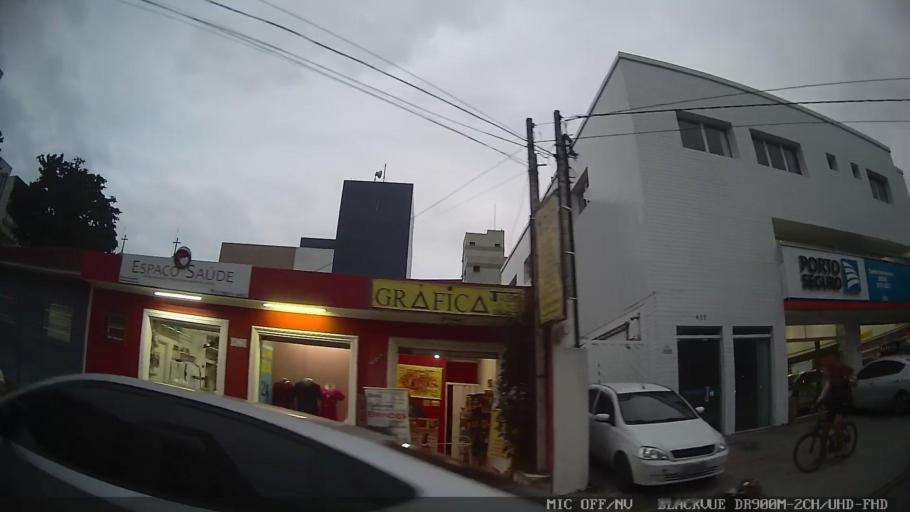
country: BR
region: Sao Paulo
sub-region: Guaruja
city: Guaruja
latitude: -23.9927
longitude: -46.2567
